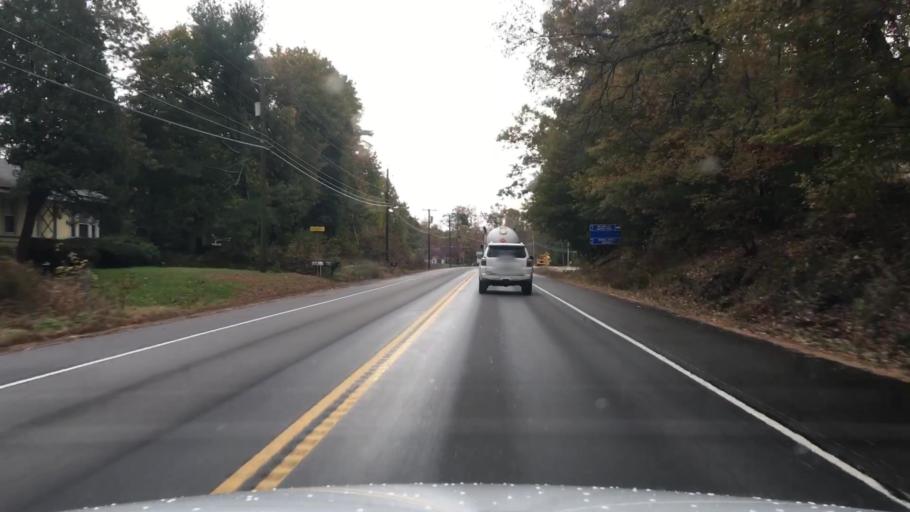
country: US
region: New Hampshire
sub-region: Strafford County
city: Lee
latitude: 43.1325
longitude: -71.0209
